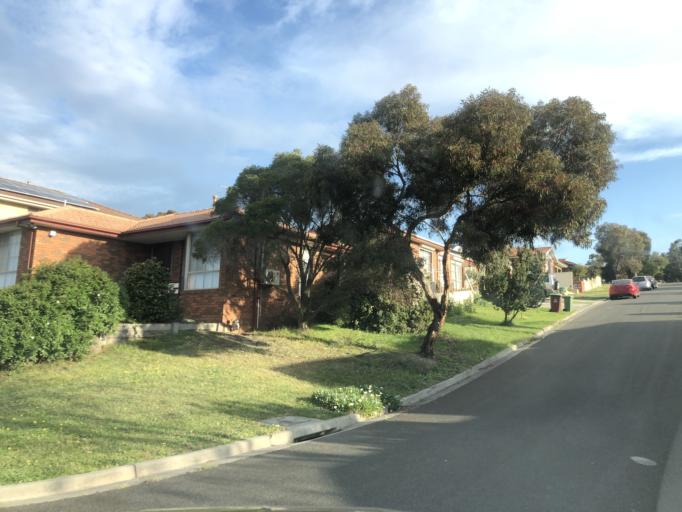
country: AU
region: Victoria
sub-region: Casey
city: Hallam
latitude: -38.0219
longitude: 145.2651
